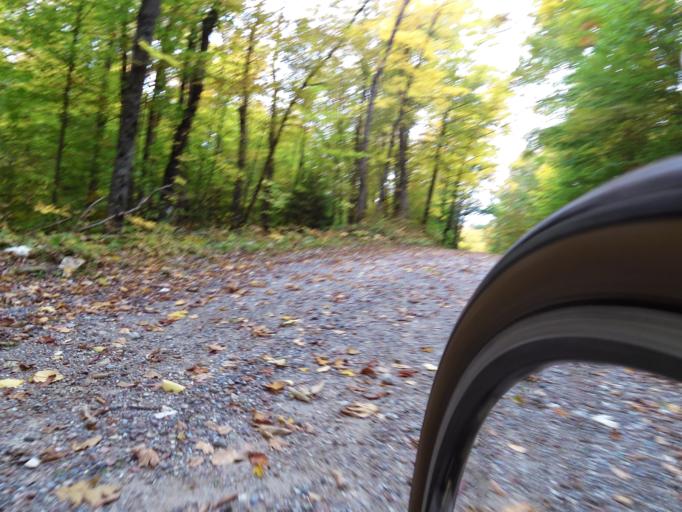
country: CA
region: Quebec
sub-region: Outaouais
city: Wakefield
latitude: 45.6016
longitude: -76.0524
